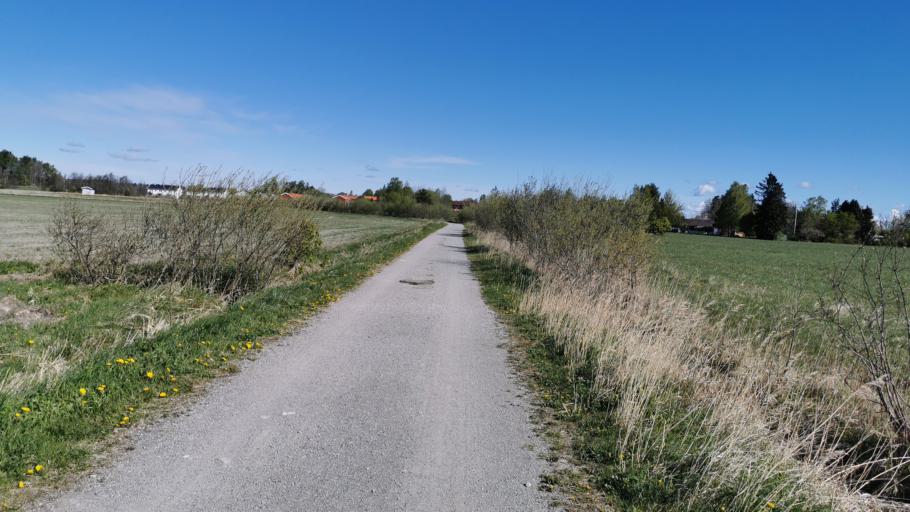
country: SE
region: OErebro
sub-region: Orebro Kommun
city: Orebro
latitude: 59.3100
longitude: 15.2158
